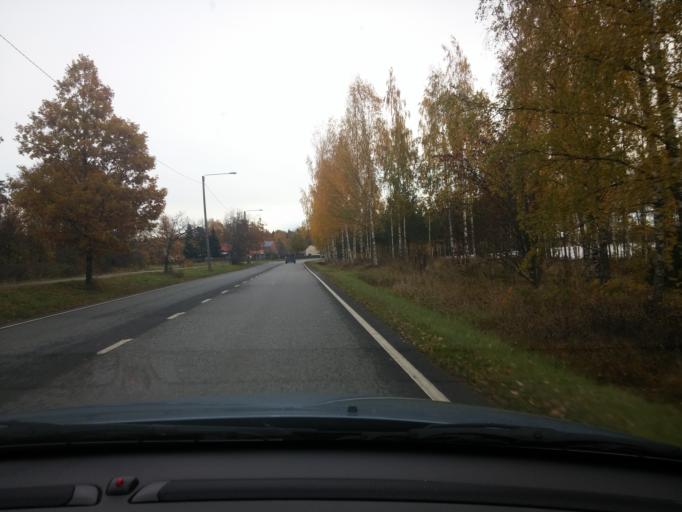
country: FI
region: Haeme
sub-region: Forssa
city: Tammela
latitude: 60.8064
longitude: 23.7917
